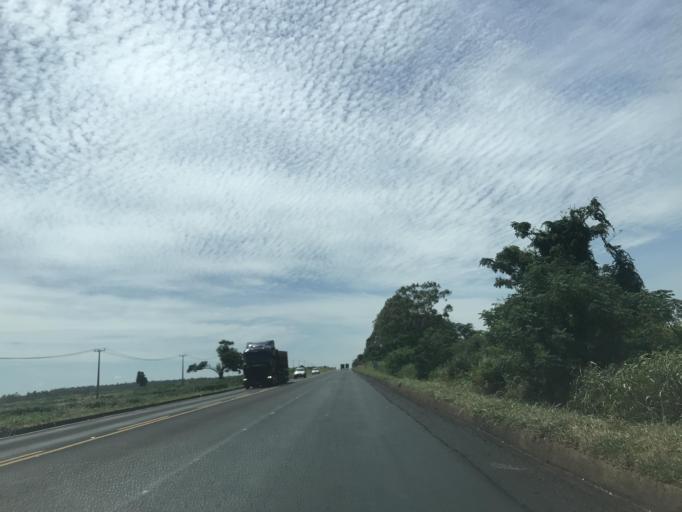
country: BR
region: Parana
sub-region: Paranavai
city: Paranavai
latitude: -23.0017
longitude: -52.5595
